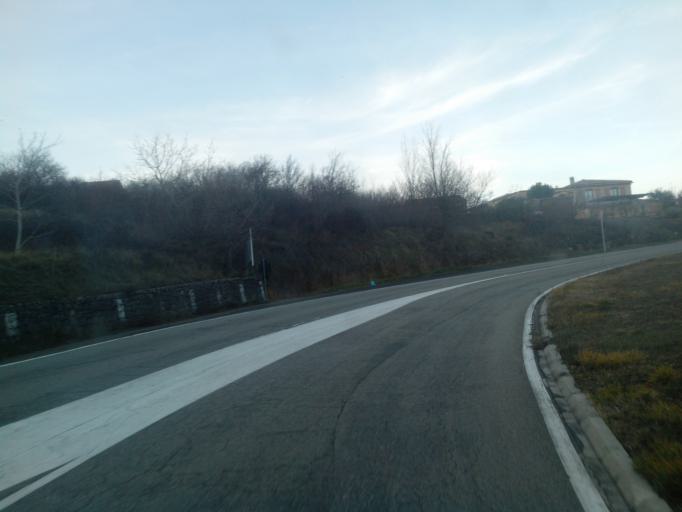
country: FR
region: Languedoc-Roussillon
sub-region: Departement de l'Aude
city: Chalabre
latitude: 42.9209
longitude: 2.0443
